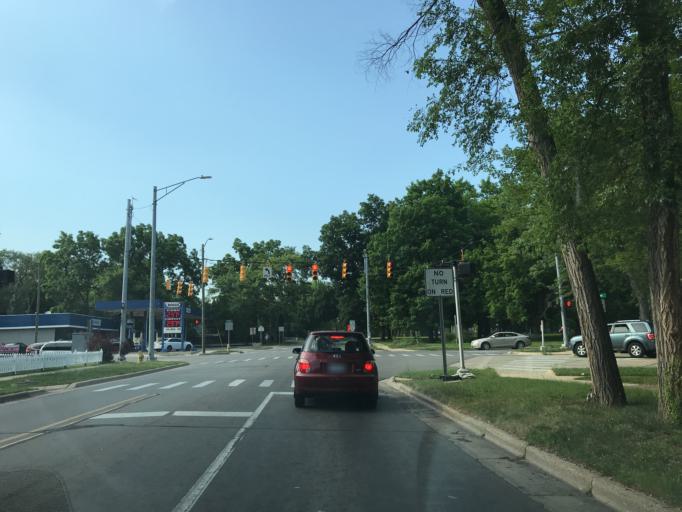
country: US
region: Michigan
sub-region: Washtenaw County
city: Ypsilanti
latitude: 42.2456
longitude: -83.6027
